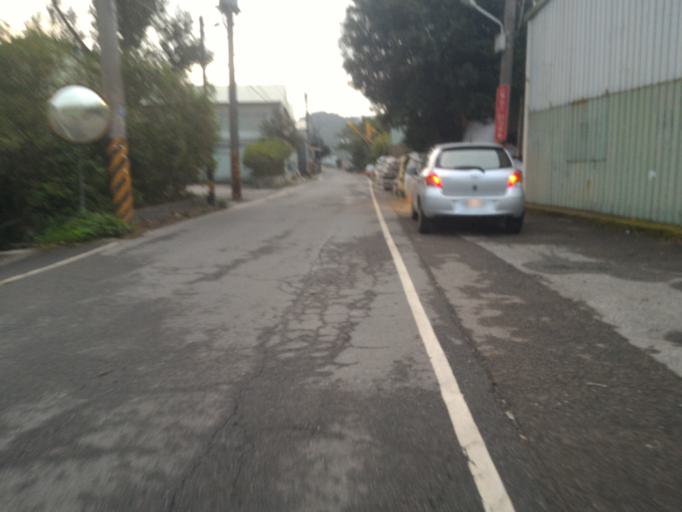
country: TW
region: Taipei
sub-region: Taipei
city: Banqiao
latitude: 24.9577
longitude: 121.4033
